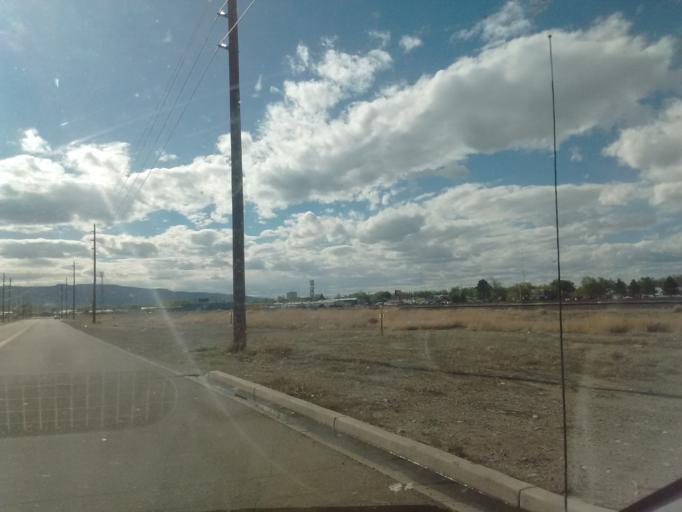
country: US
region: Colorado
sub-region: Mesa County
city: Grand Junction
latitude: 39.0630
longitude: -108.5457
